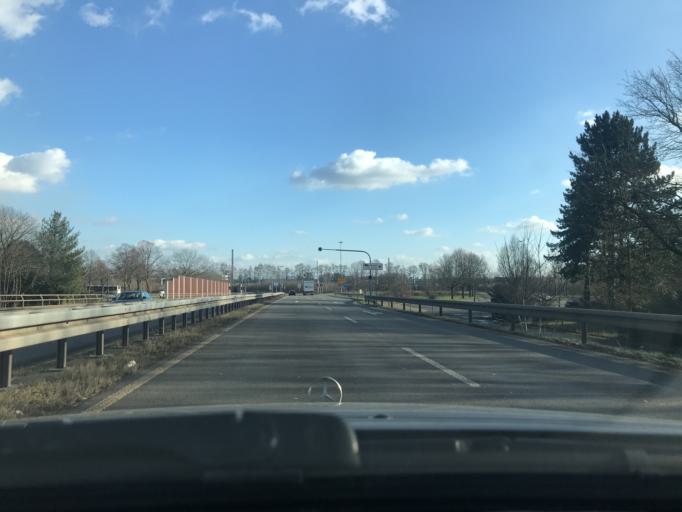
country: DE
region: North Rhine-Westphalia
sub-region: Regierungsbezirk Dusseldorf
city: Moers
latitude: 51.3860
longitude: 6.6771
